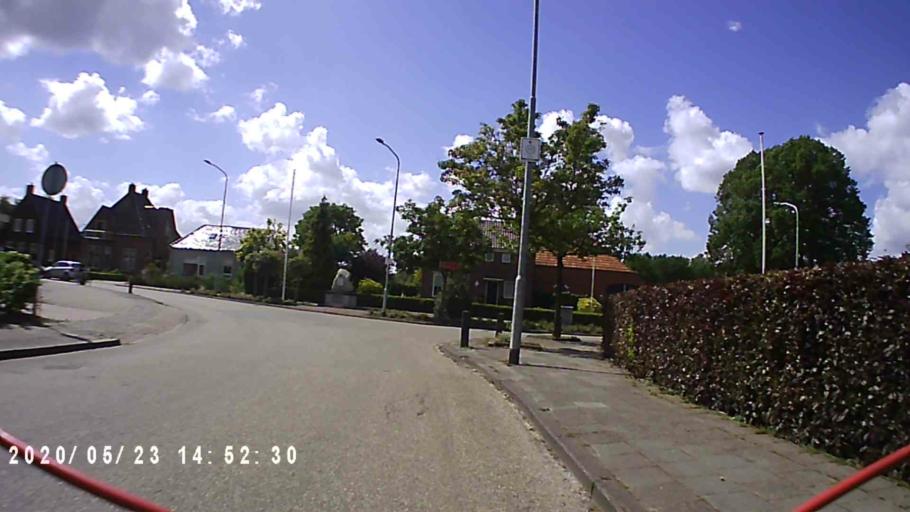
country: NL
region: Groningen
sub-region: Gemeente Delfzijl
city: Delfzijl
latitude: 53.2563
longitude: 6.9304
